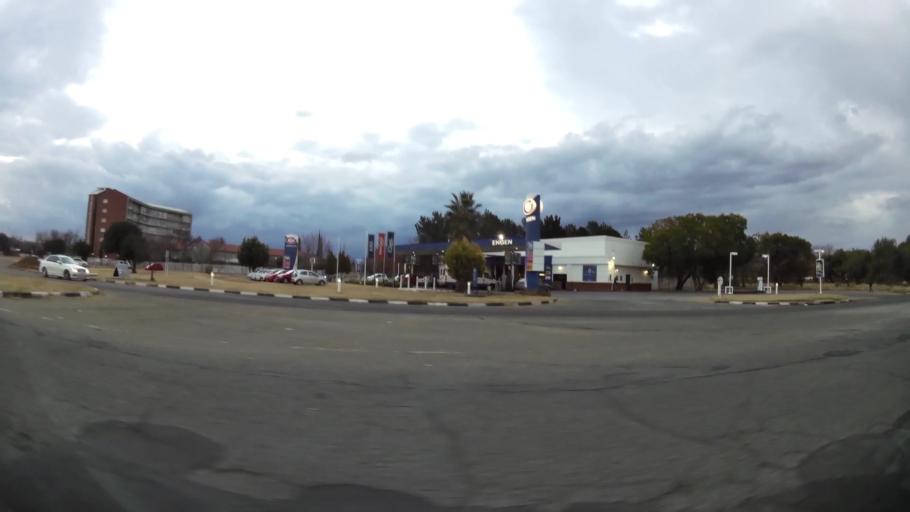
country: ZA
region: Orange Free State
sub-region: Lejweleputswa District Municipality
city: Welkom
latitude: -27.9648
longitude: 26.7505
